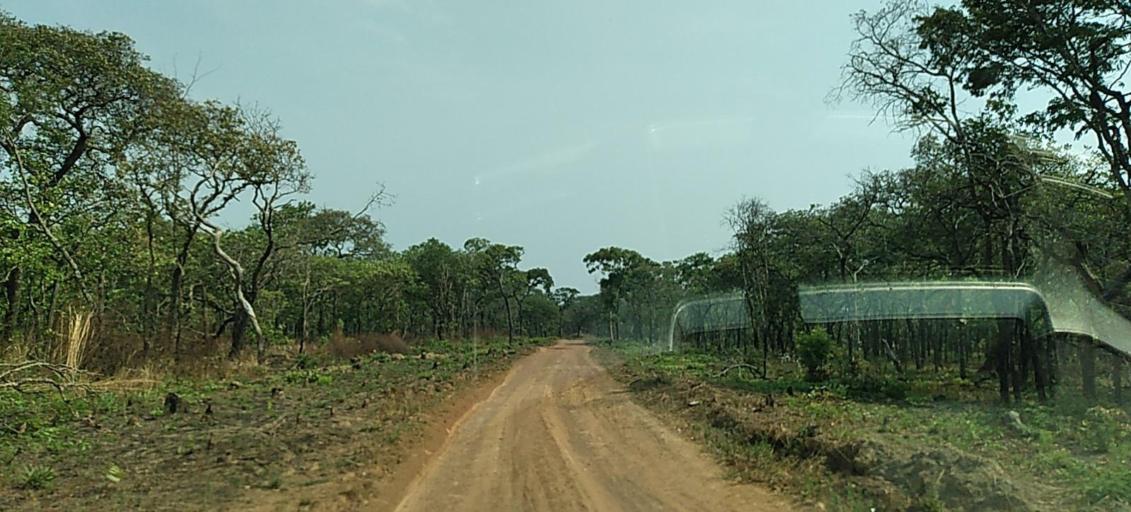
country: ZM
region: North-Western
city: Kansanshi
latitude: -12.0903
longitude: 26.8884
